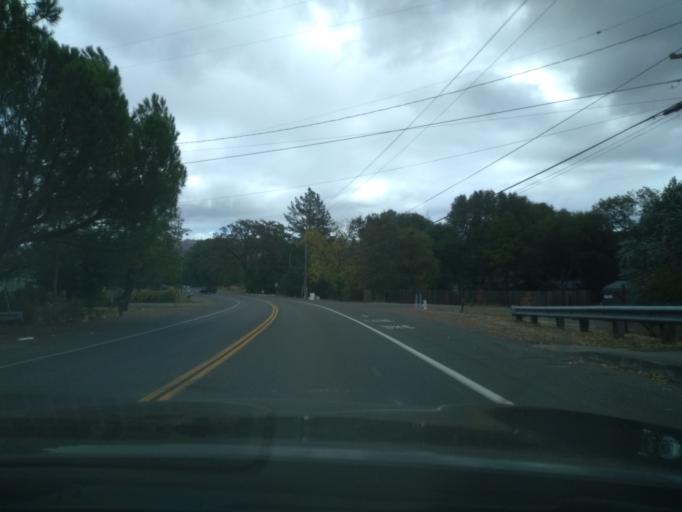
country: US
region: California
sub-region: Mendocino County
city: Ukiah
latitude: 39.1956
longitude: -123.1944
